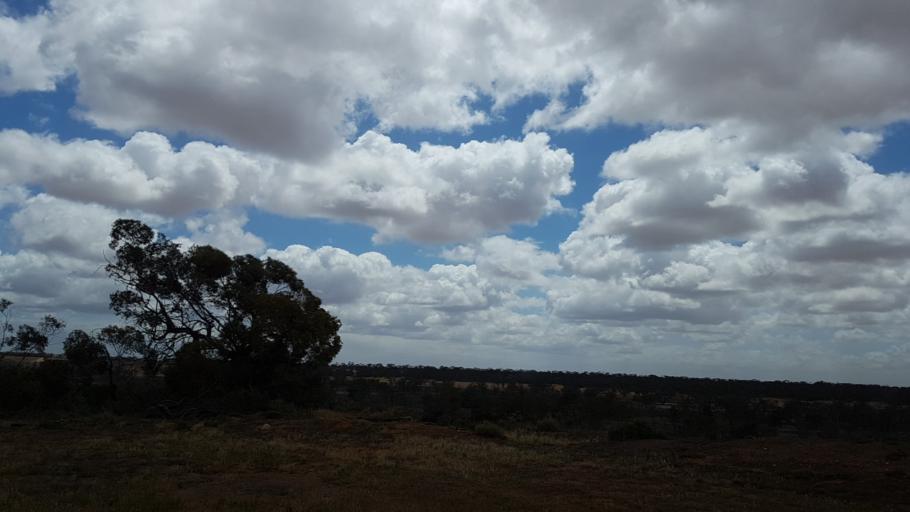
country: AU
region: South Australia
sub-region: Loxton Waikerie
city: Waikerie
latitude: -34.1688
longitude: 140.0377
